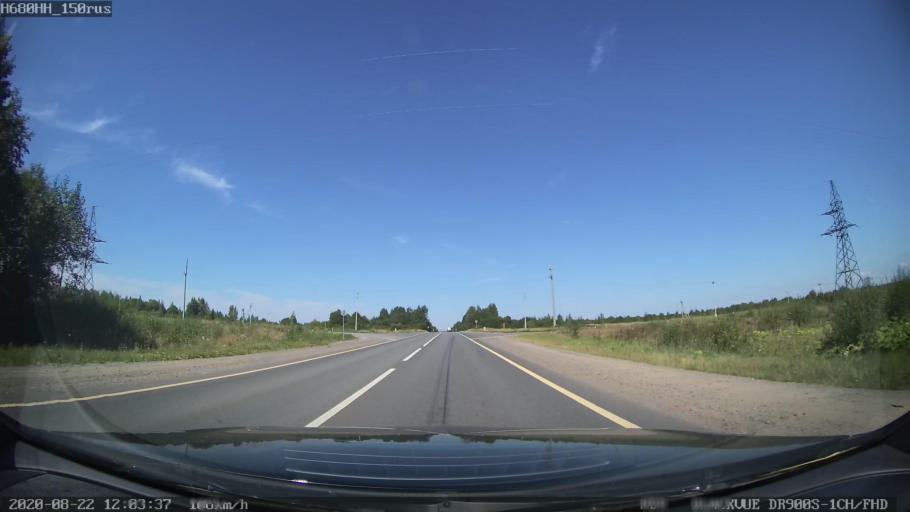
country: RU
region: Tverskaya
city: Rameshki
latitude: 57.2573
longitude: 36.0829
